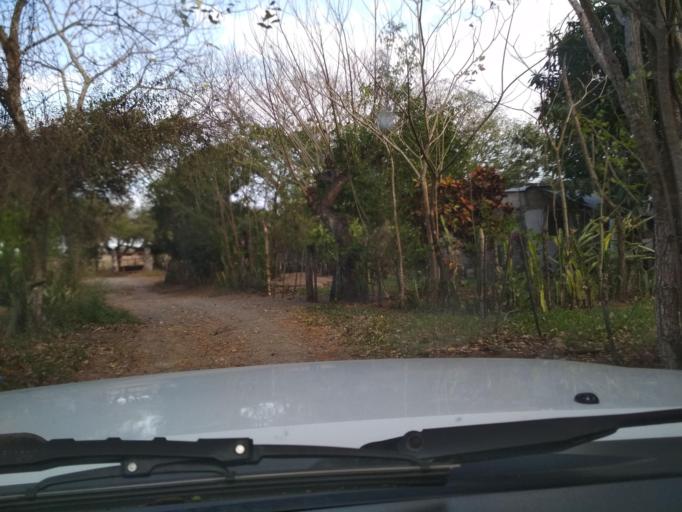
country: MX
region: Veracruz
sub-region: Veracruz
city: Delfino Victoria (Santa Fe)
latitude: 19.1504
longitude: -96.2971
